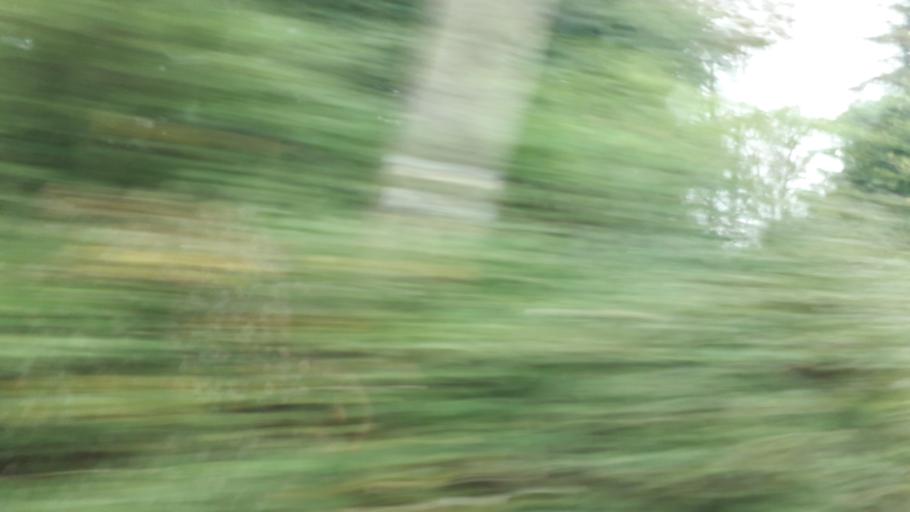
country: IE
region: Connaught
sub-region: Roscommon
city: Ballaghaderreen
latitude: 53.8867
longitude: -8.5378
